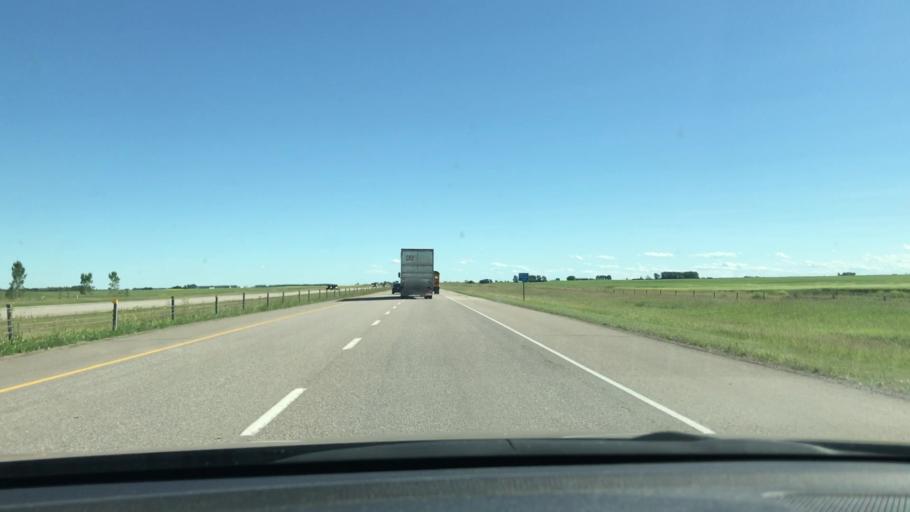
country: CA
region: Alberta
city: Olds
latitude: 51.7028
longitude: -114.0256
